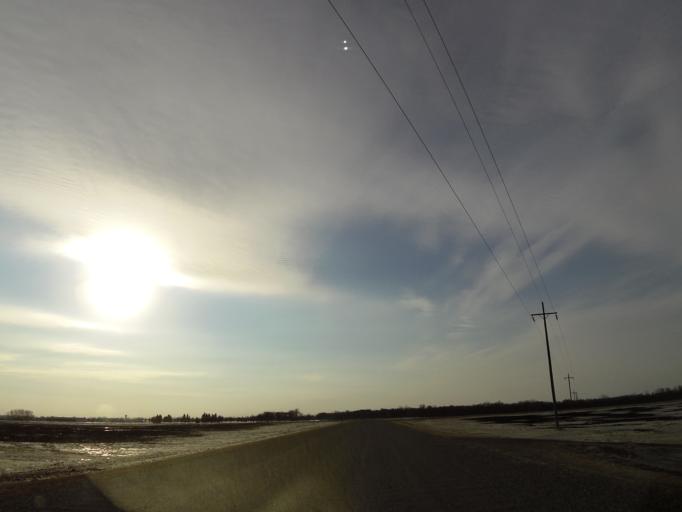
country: US
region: North Dakota
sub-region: Walsh County
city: Grafton
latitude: 48.4198
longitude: -97.3749
